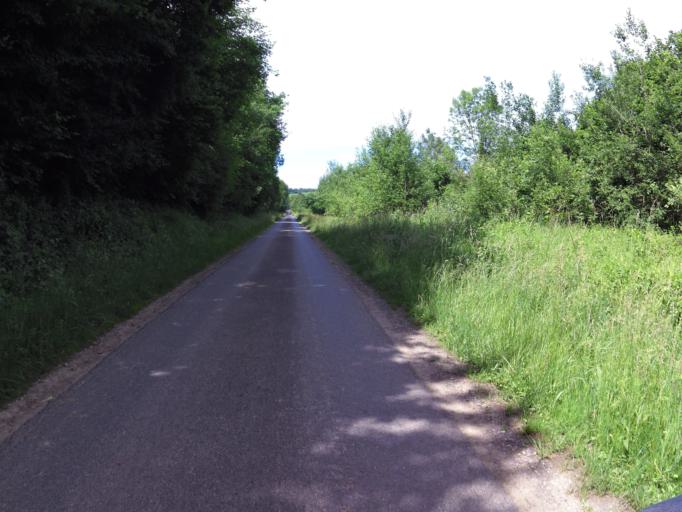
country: FR
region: Champagne-Ardenne
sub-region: Departement des Ardennes
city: Mouzon
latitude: 49.5379
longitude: 5.0868
